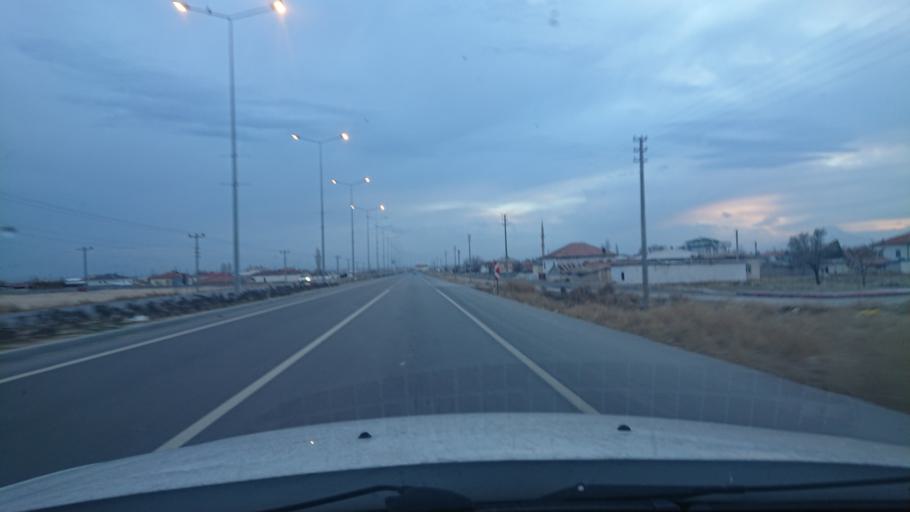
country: TR
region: Aksaray
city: Sultanhani
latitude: 38.2518
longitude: 33.5492
